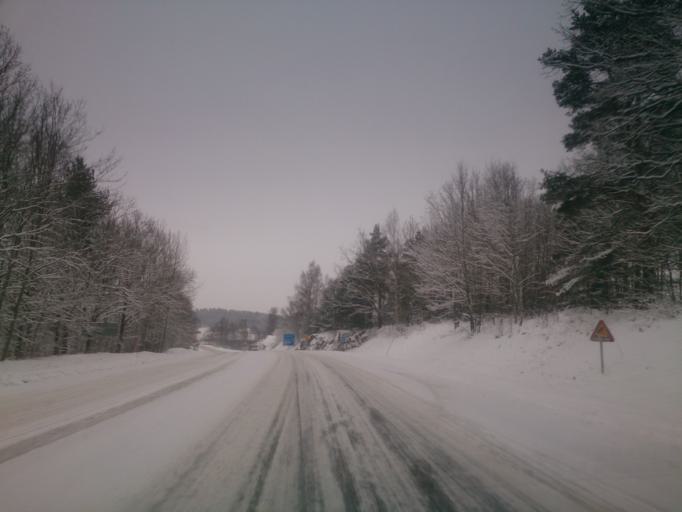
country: SE
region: OEstergoetland
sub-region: Norrkopings Kommun
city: Kimstad
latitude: 58.5063
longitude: 15.9818
